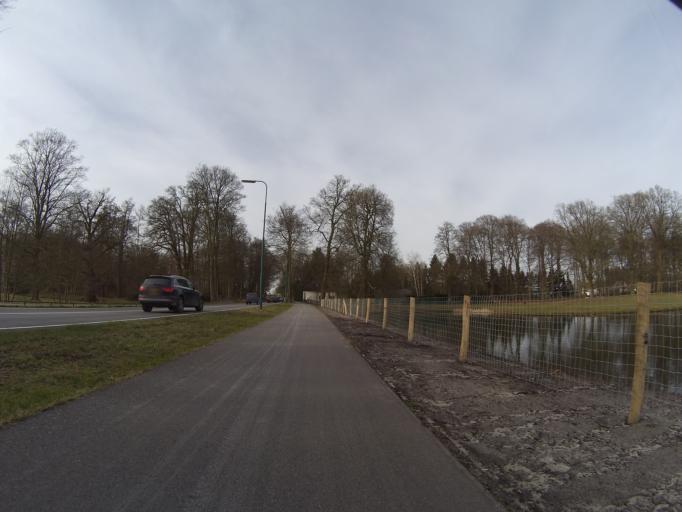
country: NL
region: Utrecht
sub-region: Gemeente Amersfoort
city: Randenbroek
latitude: 52.1390
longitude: 5.4103
